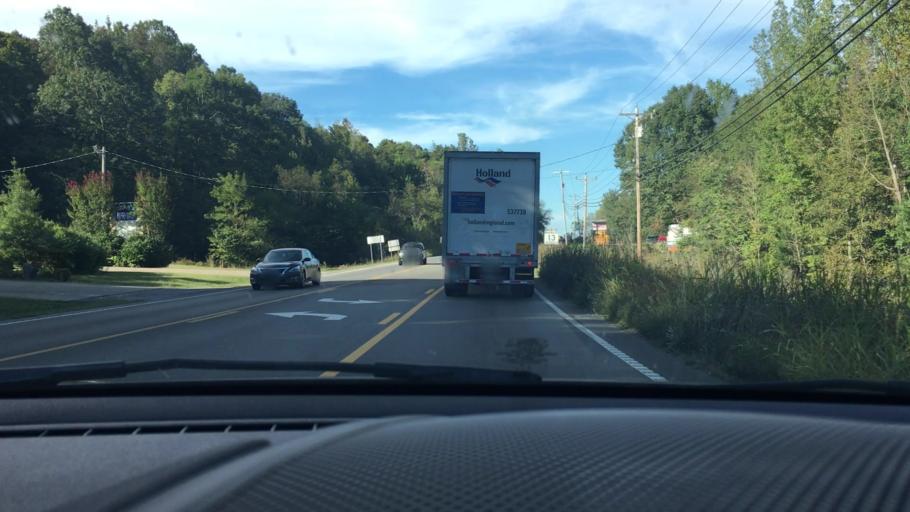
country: US
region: Tennessee
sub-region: Montgomery County
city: Clarksville
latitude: 36.4742
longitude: -87.3770
